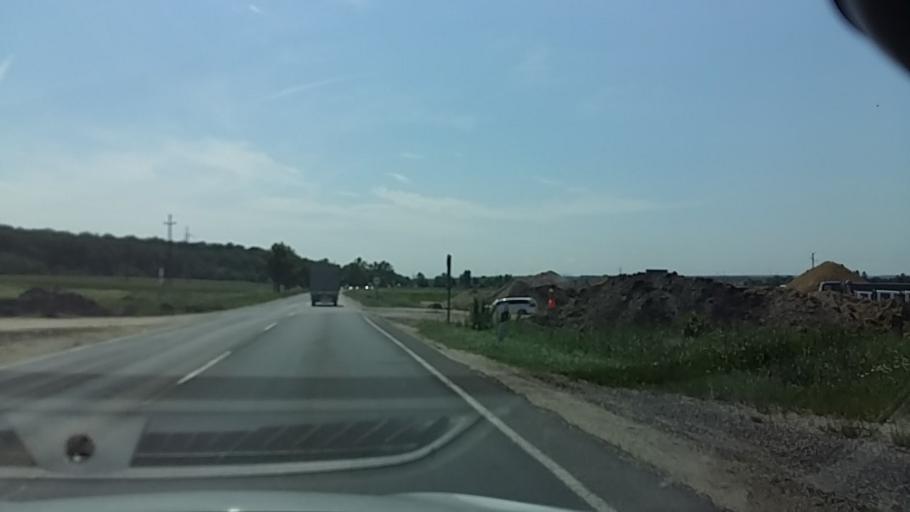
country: HU
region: Gyor-Moson-Sopron
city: Sopron
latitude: 47.6590
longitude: 16.6266
